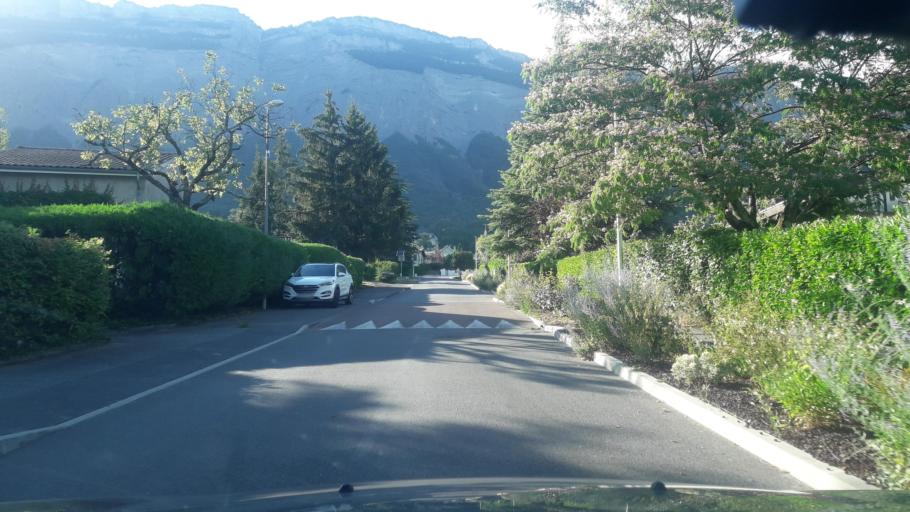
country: FR
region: Rhone-Alpes
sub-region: Departement de l'Isere
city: Biviers
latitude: 45.2338
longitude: 5.8062
